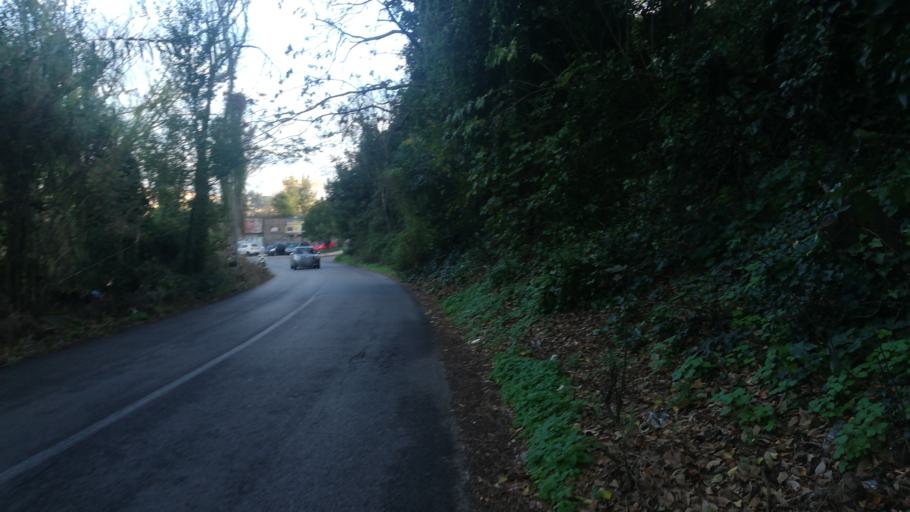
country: IT
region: Latium
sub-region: Citta metropolitana di Roma Capitale
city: Rome
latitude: 41.9275
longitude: 12.5288
